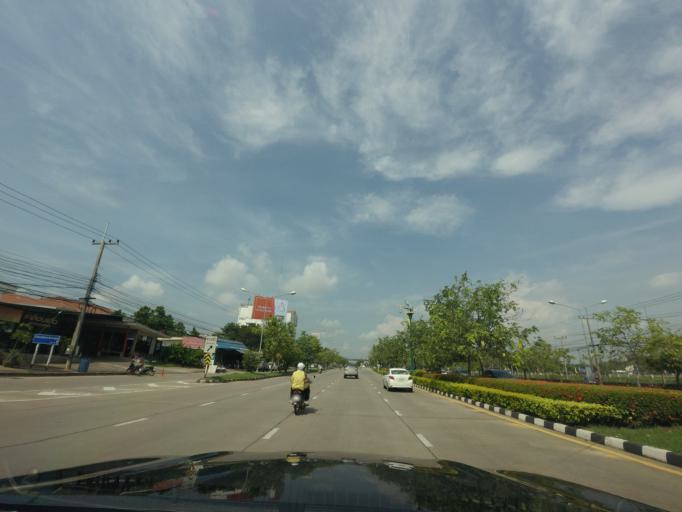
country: TH
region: Khon Kaen
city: Khon Kaen
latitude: 16.4413
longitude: 102.8168
